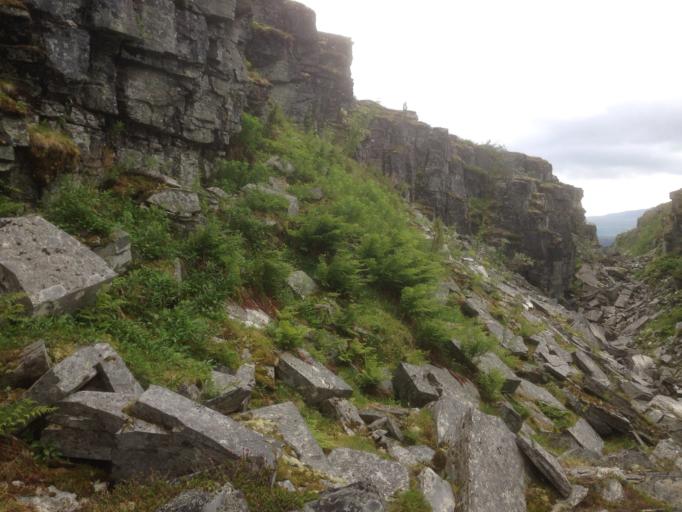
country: SE
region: Jaemtland
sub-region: Are Kommun
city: Are
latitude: 62.6943
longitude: 12.9399
